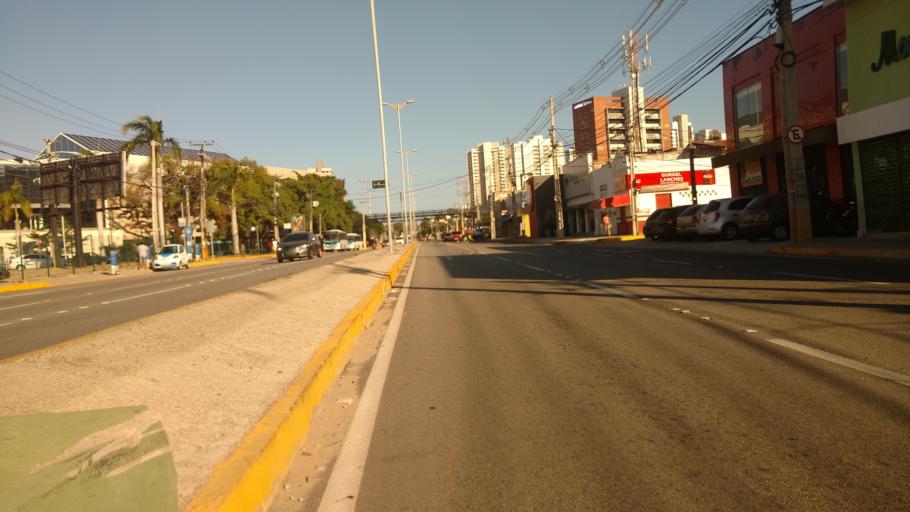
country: BR
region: Ceara
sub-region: Fortaleza
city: Fortaleza
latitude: -3.7572
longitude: -38.4905
